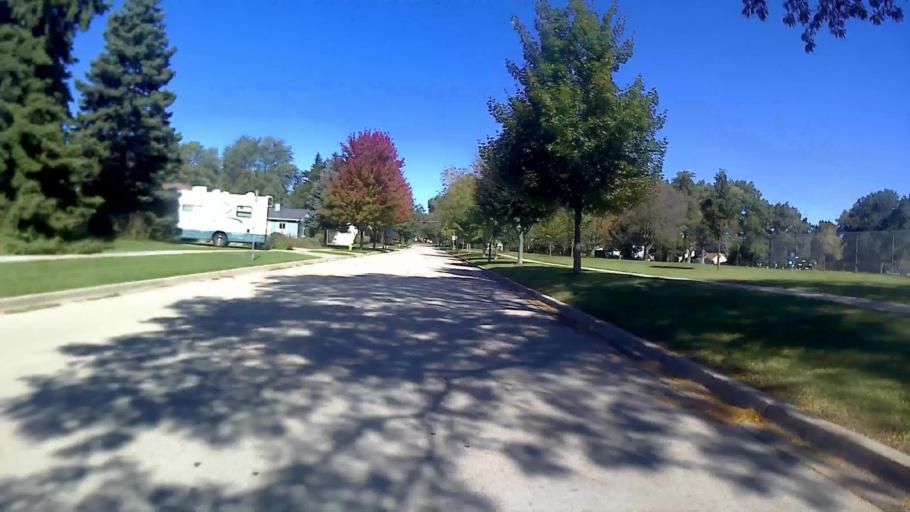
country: US
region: Illinois
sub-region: DuPage County
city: Lombard
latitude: 41.8953
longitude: -88.0254
